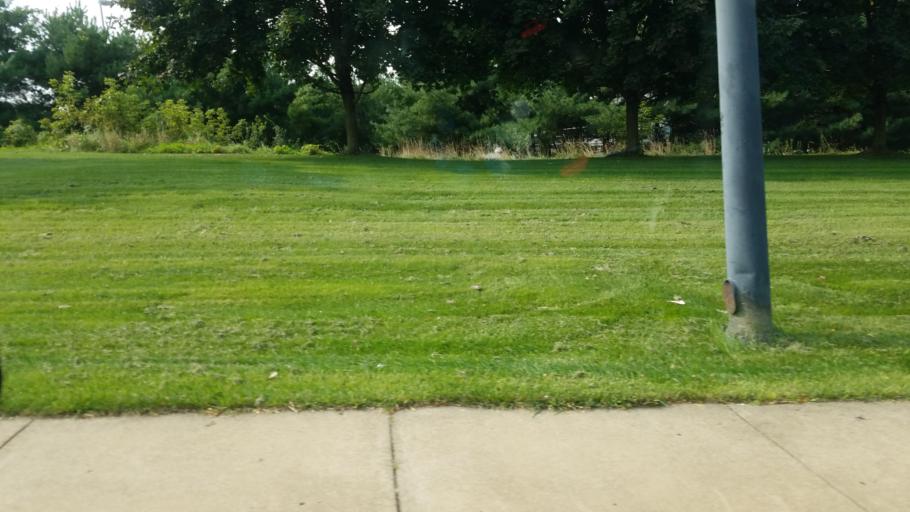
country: US
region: Ohio
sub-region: Mahoning County
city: Youngstown
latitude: 41.0965
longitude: -80.6466
